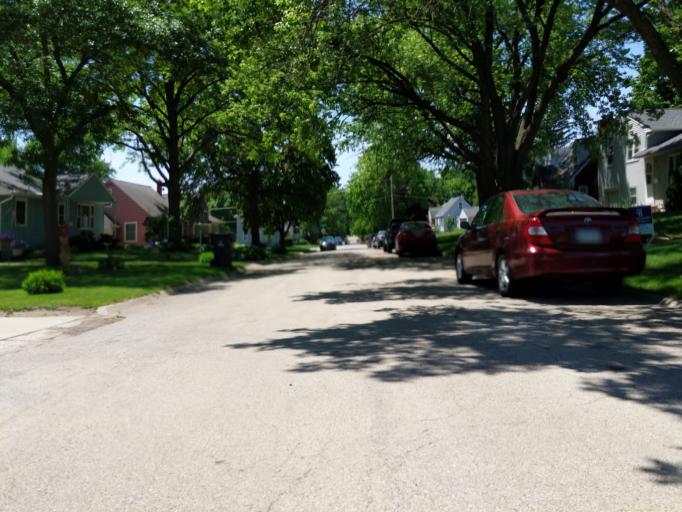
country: US
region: Iowa
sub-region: Linn County
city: Cedar Rapids
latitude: 42.0203
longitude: -91.6374
